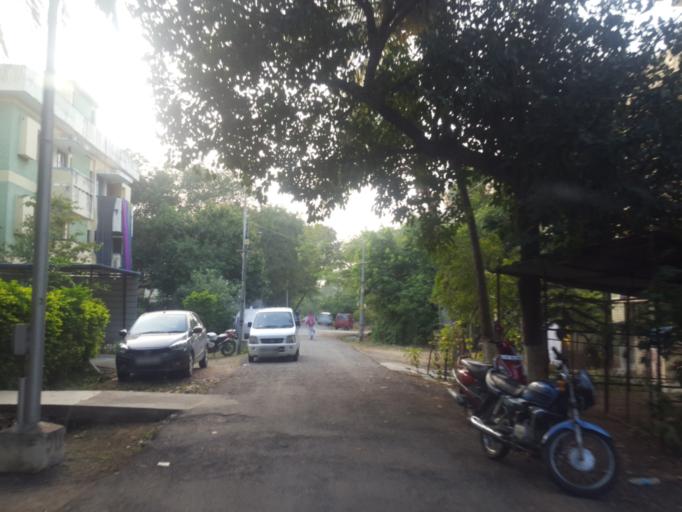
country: IN
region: Telangana
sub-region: Rangareddi
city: Singapur
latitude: 17.4672
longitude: 78.1636
